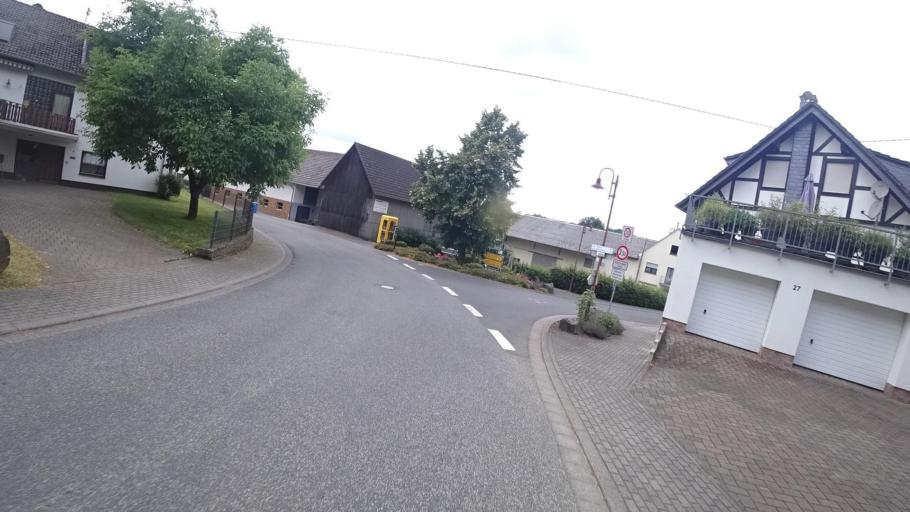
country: DE
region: Rheinland-Pfalz
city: Birnbach
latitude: 50.7033
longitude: 7.5855
